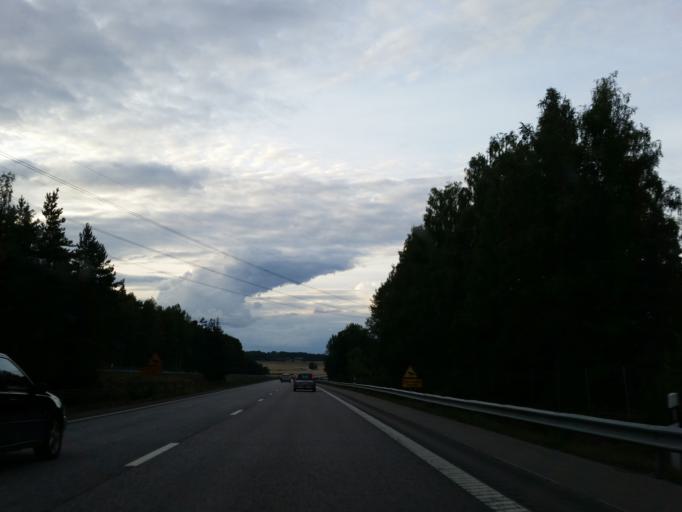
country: SE
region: Uppsala
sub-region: Uppsala Kommun
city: Alsike
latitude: 59.8017
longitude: 17.7673
